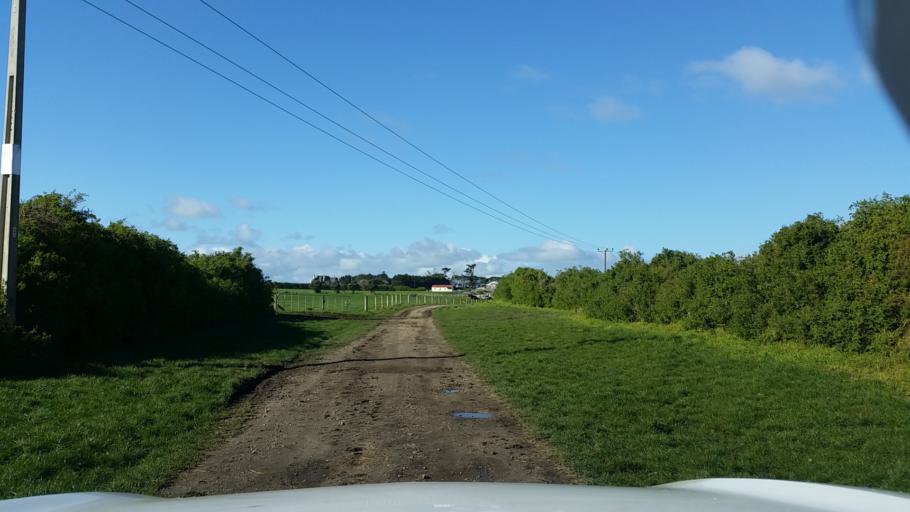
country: NZ
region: Taranaki
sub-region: South Taranaki District
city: Hawera
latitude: -39.6595
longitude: 174.3609
